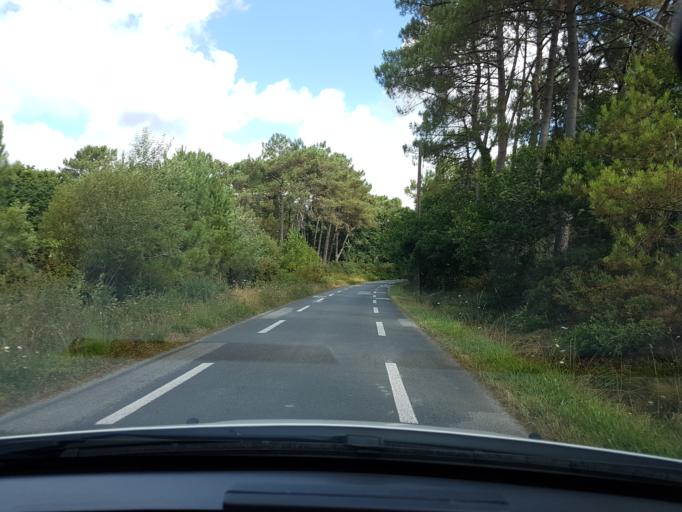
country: FR
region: Brittany
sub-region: Departement du Morbihan
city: Sainte-Helene
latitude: 47.7134
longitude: -3.1947
